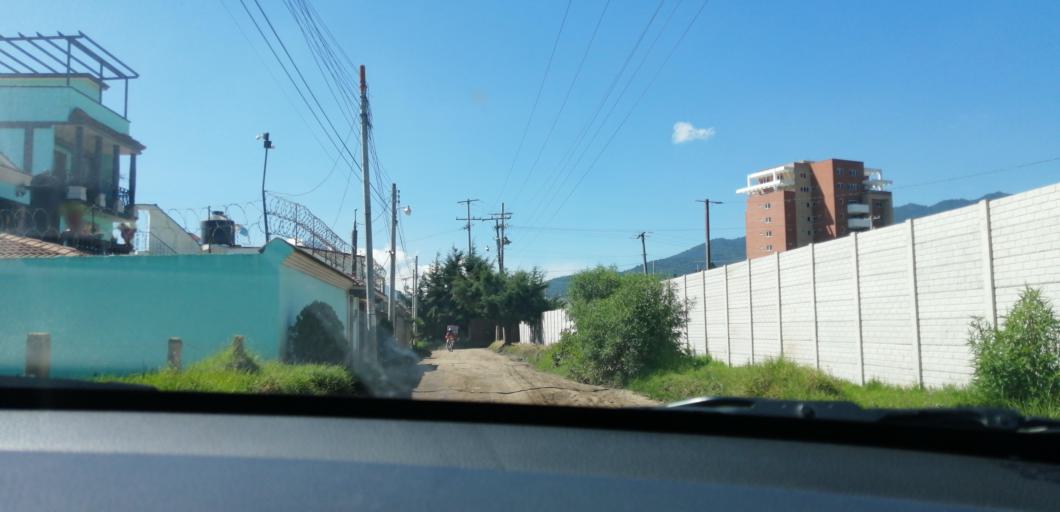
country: GT
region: Quetzaltenango
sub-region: Municipio de La Esperanza
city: La Esperanza
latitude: 14.8652
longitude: -91.5506
